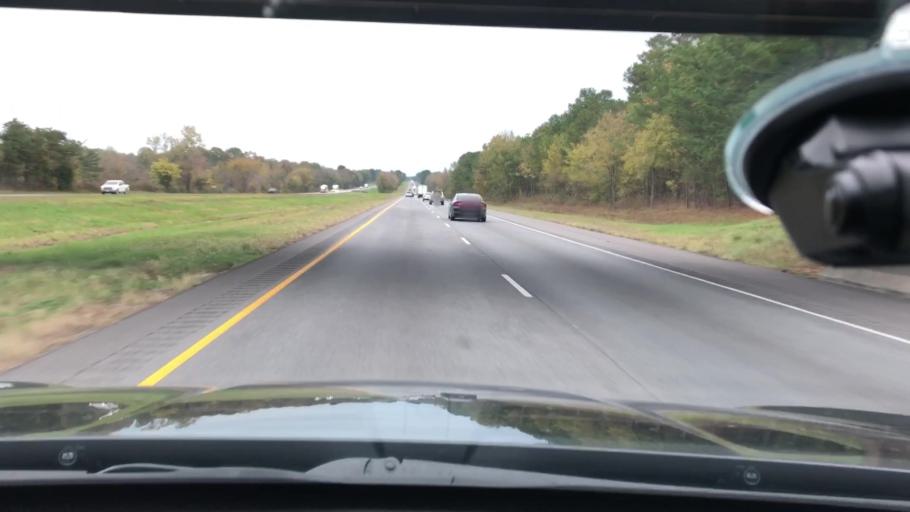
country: US
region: Arkansas
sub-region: Hempstead County
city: Hope
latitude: 33.6235
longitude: -93.7672
